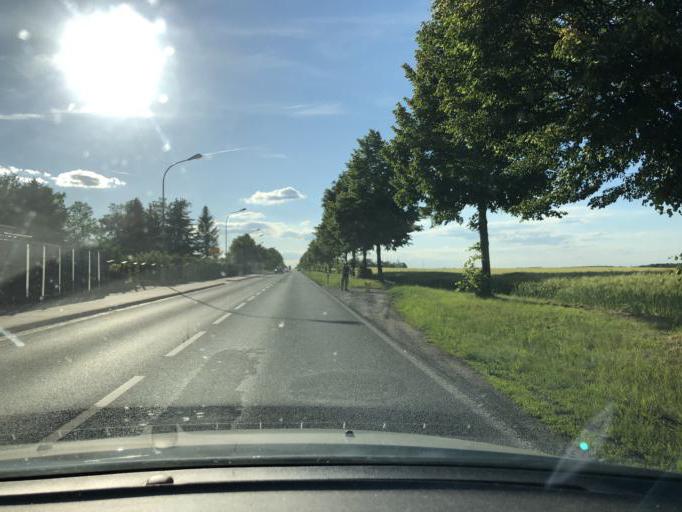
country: DE
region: Thuringia
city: Kriebitzsch
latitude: 51.0309
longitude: 12.3358
